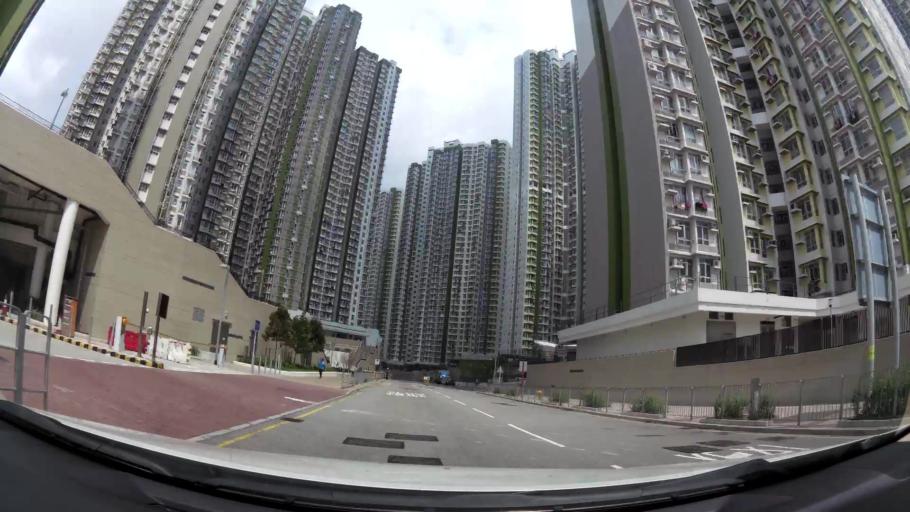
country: HK
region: Kowloon City
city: Kowloon
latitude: 22.3198
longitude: 114.2363
